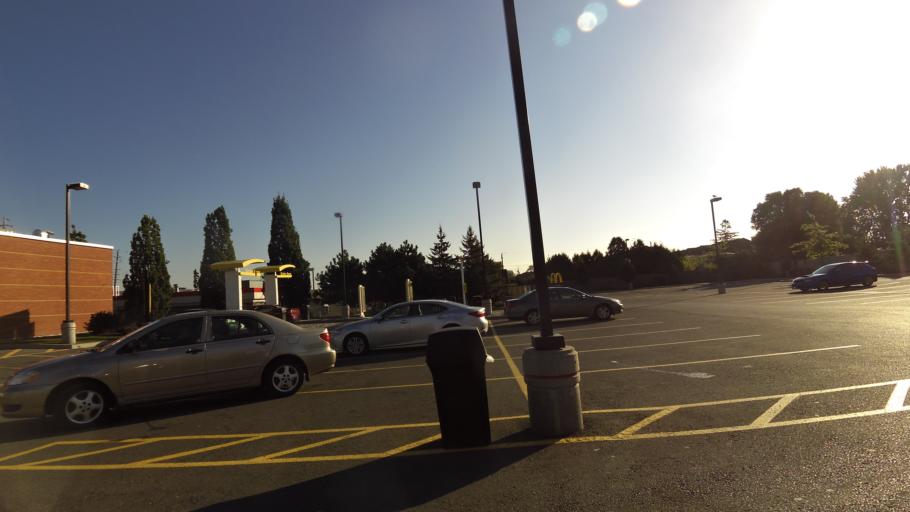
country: CA
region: Ontario
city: Ottawa
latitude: 45.4487
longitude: -75.5891
